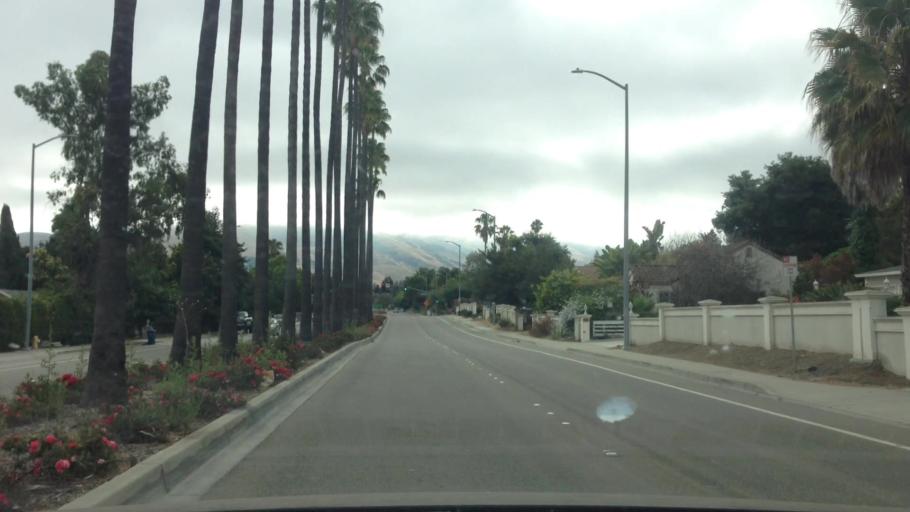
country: US
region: California
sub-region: Alameda County
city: Fremont
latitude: 37.5327
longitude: -121.9476
